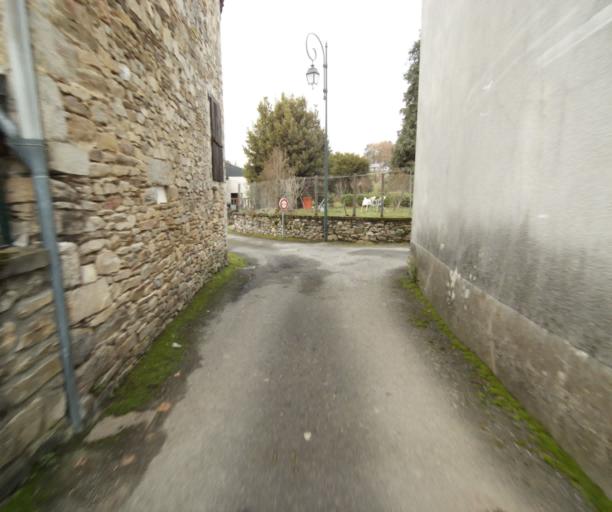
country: FR
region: Limousin
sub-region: Departement de la Correze
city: Chameyrat
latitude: 45.2332
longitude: 1.7002
